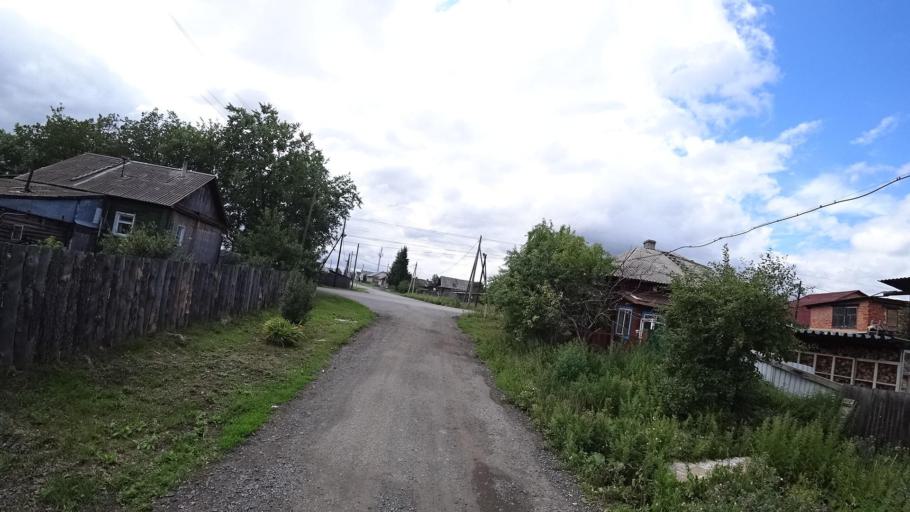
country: RU
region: Sverdlovsk
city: Kamyshlov
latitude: 56.8585
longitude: 62.7080
